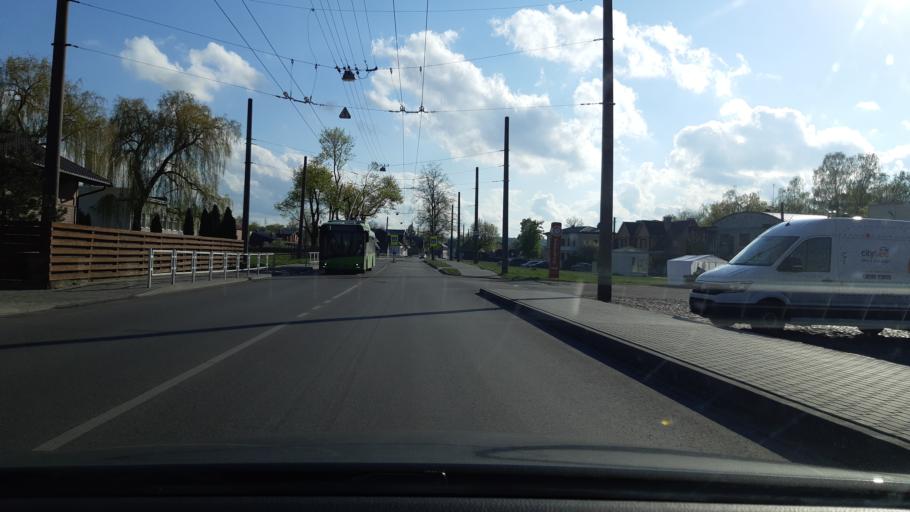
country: LT
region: Kauno apskritis
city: Dainava (Kaunas)
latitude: 54.8640
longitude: 23.9647
